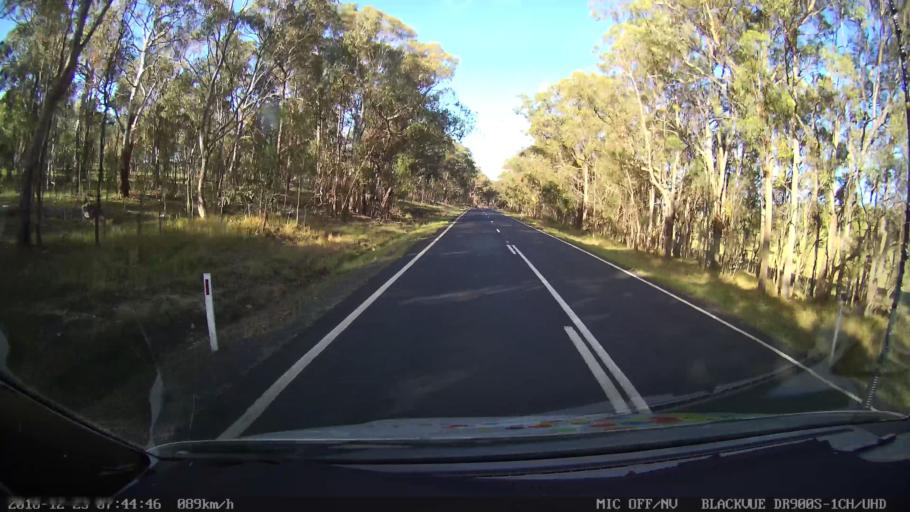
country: AU
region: New South Wales
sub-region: Armidale Dumaresq
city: Enmore
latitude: -30.5250
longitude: 151.9453
